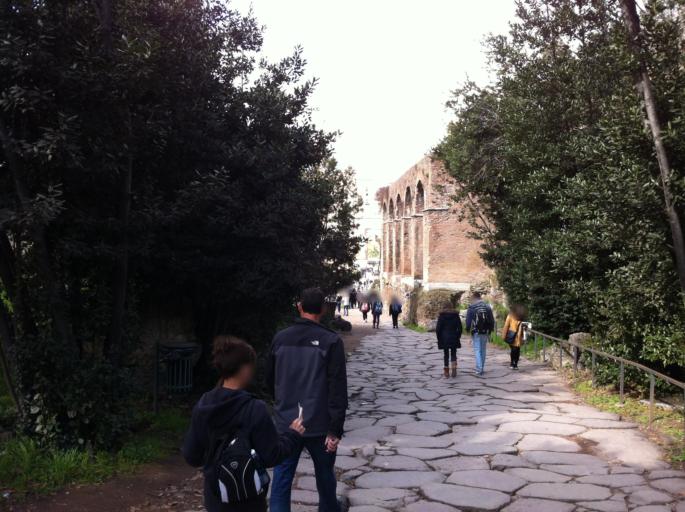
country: IT
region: Latium
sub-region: Citta metropolitana di Roma Capitale
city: Rome
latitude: 41.8914
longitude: 12.4879
